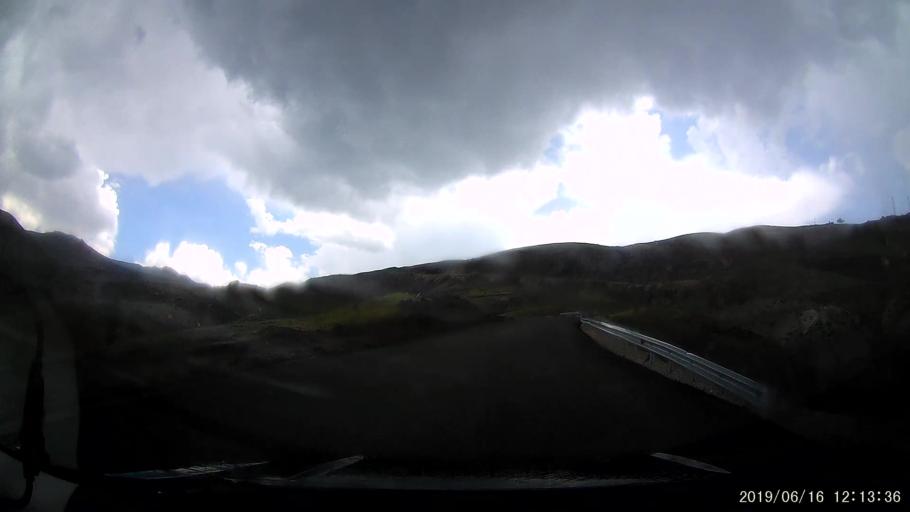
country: TR
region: Agri
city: Dogubayazit
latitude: 39.4477
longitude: 44.2396
